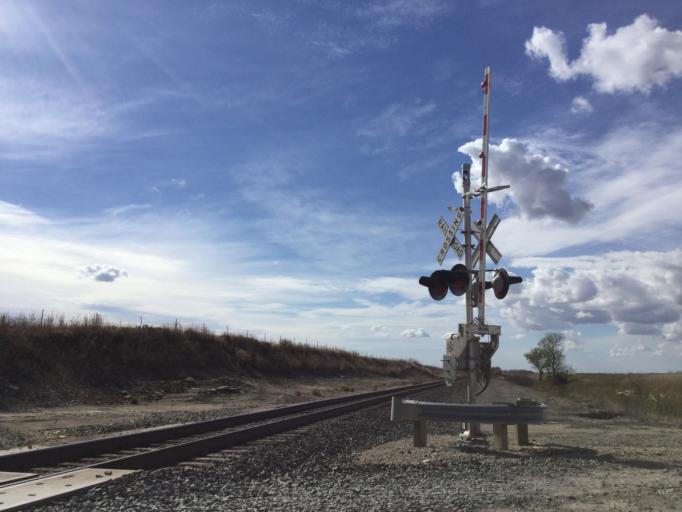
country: US
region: Kansas
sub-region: Butler County
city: El Dorado
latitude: 37.9557
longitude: -96.7193
